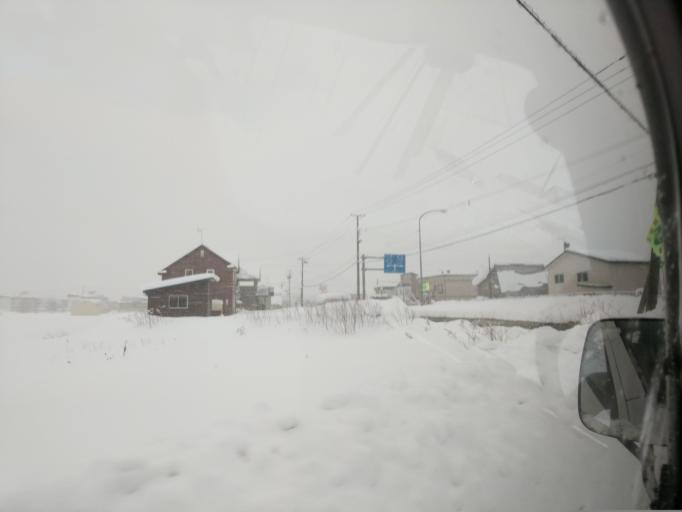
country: JP
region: Hokkaido
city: Niseko Town
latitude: 42.8901
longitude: 140.7453
